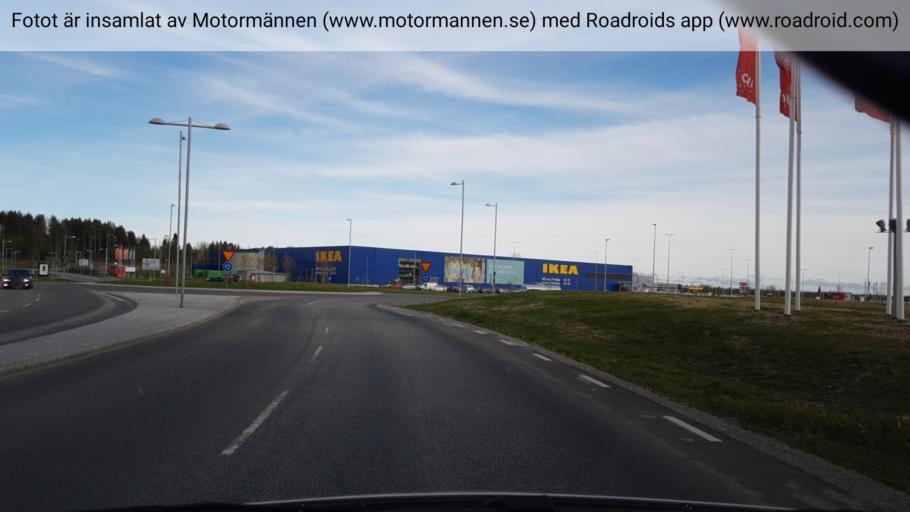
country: SE
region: Vaesterbotten
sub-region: Umea Kommun
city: Umea
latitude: 63.8107
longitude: 20.2511
